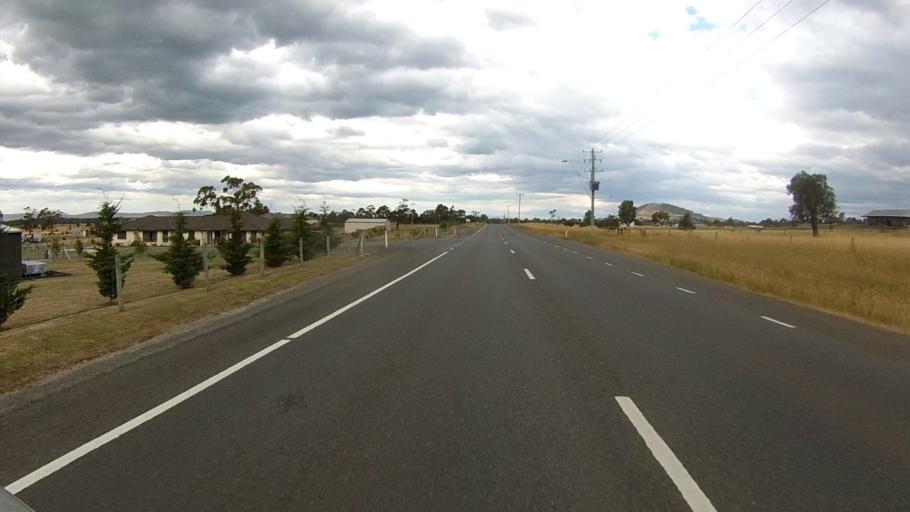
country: AU
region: Tasmania
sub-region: Clarence
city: Cambridge
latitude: -42.8401
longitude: 147.4681
